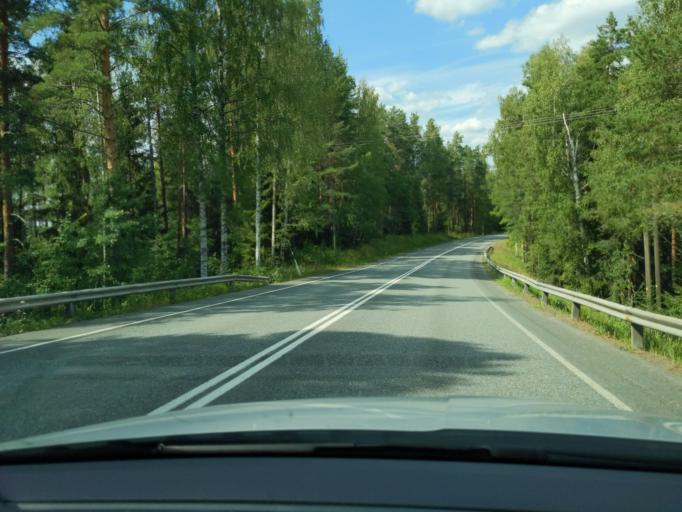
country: FI
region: Paijanne Tavastia
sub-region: Lahti
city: Heinola
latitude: 61.2832
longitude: 26.0645
